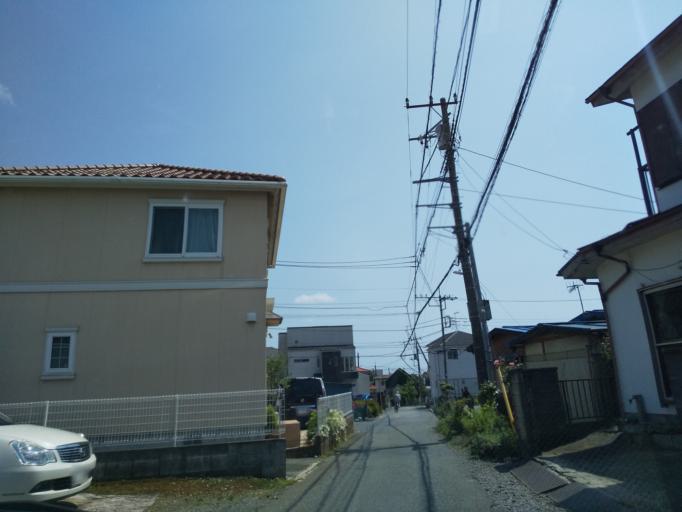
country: JP
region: Kanagawa
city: Zama
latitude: 35.5028
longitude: 139.3905
